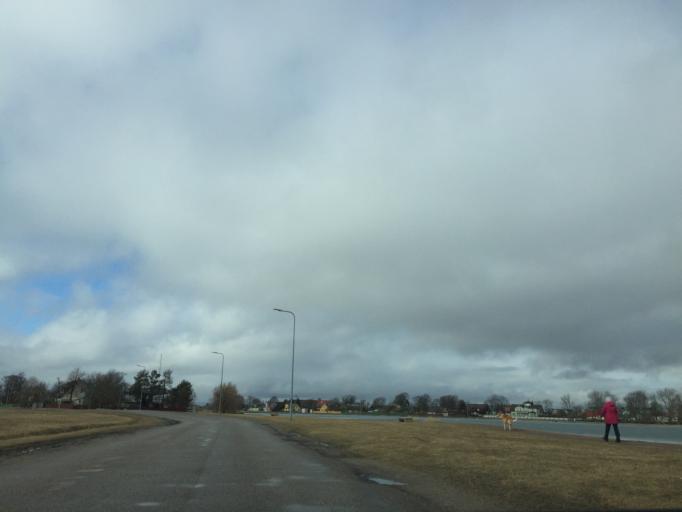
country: EE
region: Laeaene
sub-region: Haapsalu linn
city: Haapsalu
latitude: 58.9510
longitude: 23.5266
